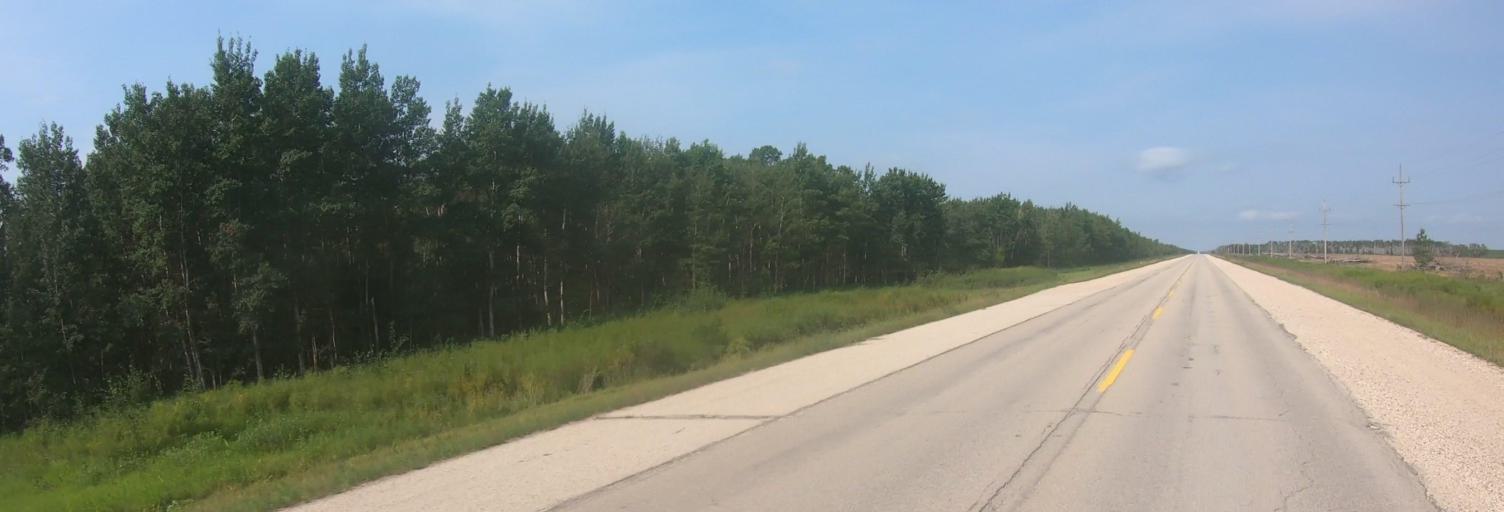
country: CA
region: Manitoba
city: Steinbach
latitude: 49.3308
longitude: -96.6089
